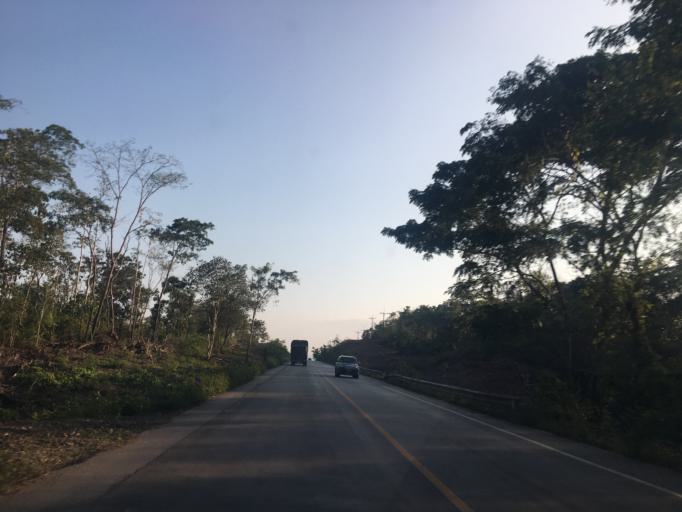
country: TH
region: Lampang
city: Ngao
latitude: 18.6528
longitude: 100.0177
